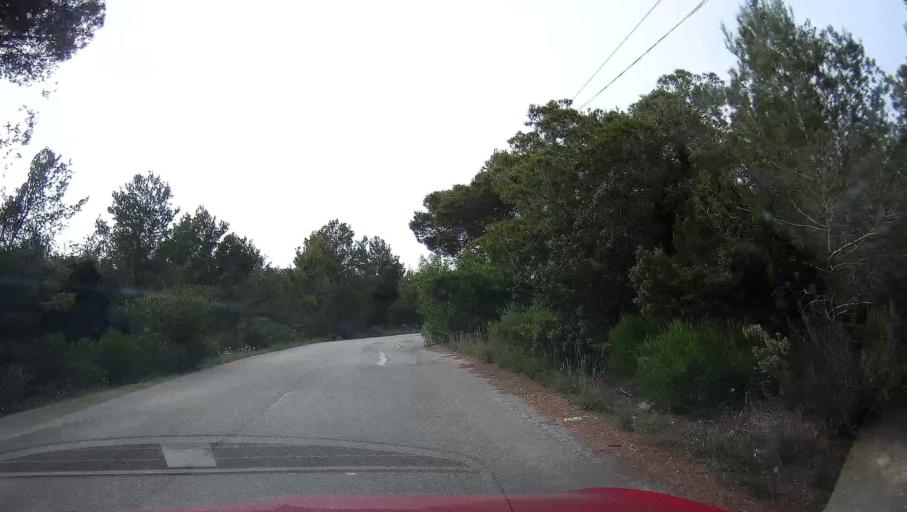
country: ES
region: Balearic Islands
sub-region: Illes Balears
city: Sant Joan de Labritja
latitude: 39.1051
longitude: 1.5124
